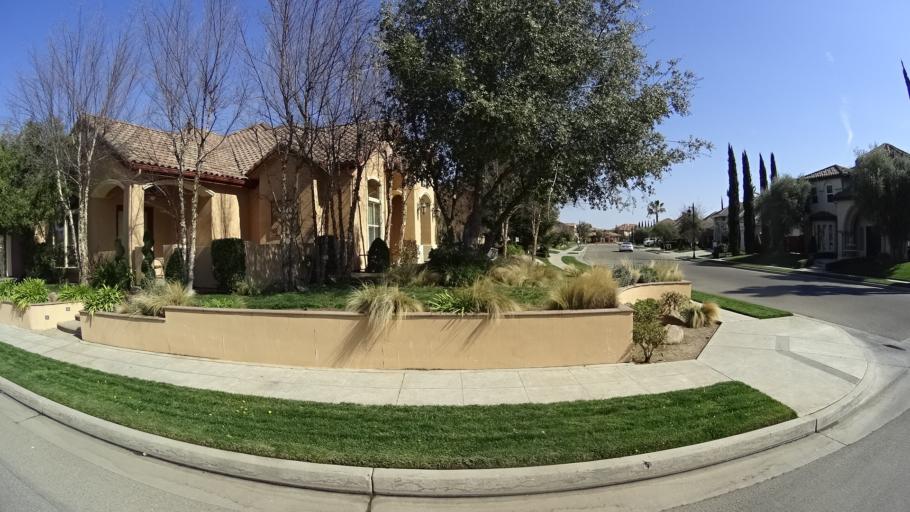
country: US
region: California
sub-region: Fresno County
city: Clovis
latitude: 36.8943
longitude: -119.7436
